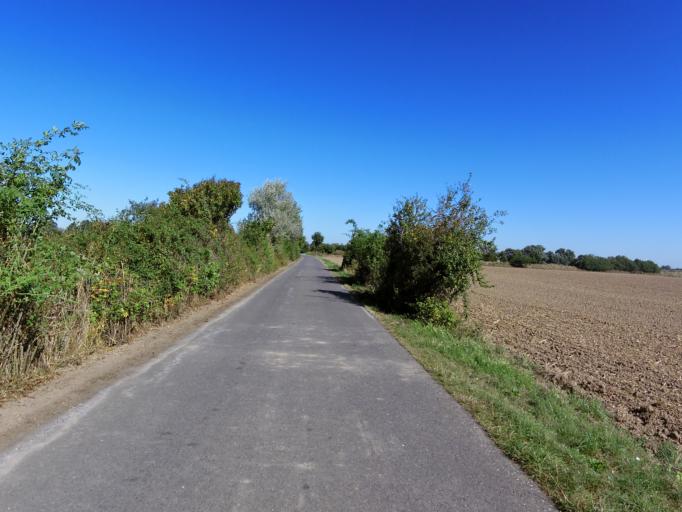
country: DE
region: Saxony
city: Elsnig
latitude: 51.6272
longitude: 12.9269
